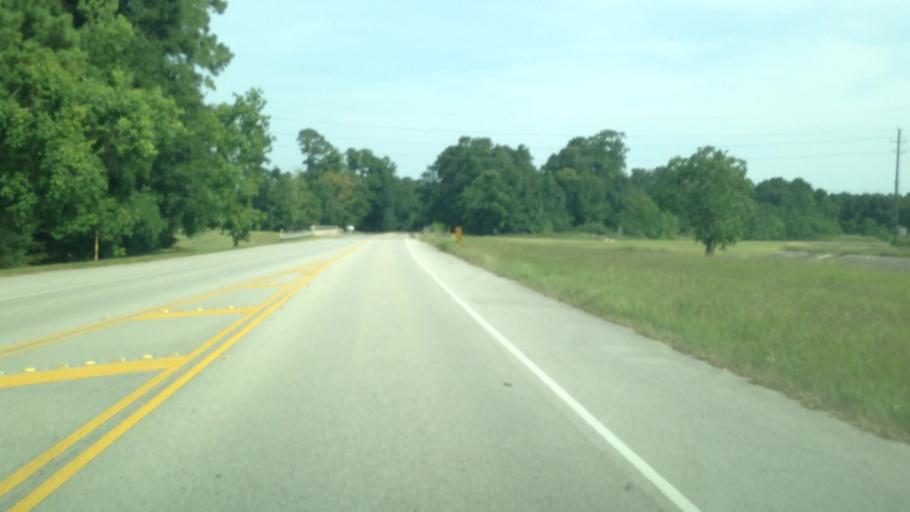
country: US
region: Texas
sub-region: Harris County
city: Sheldon
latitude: 29.9212
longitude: -95.1661
